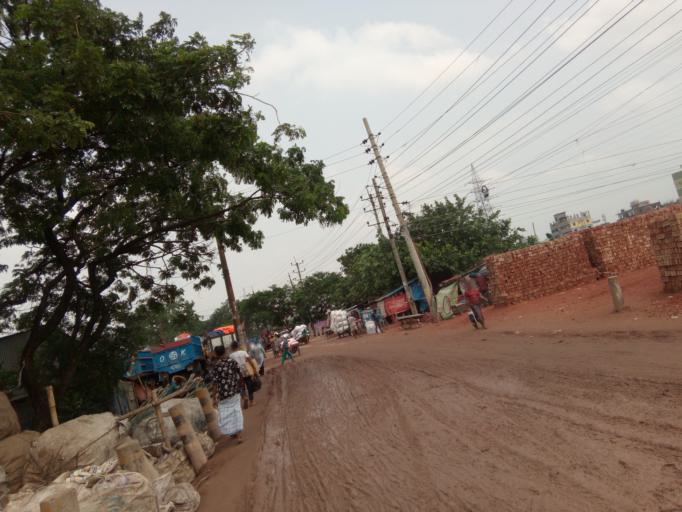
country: BD
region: Dhaka
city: Azimpur
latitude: 23.7141
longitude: 90.3835
